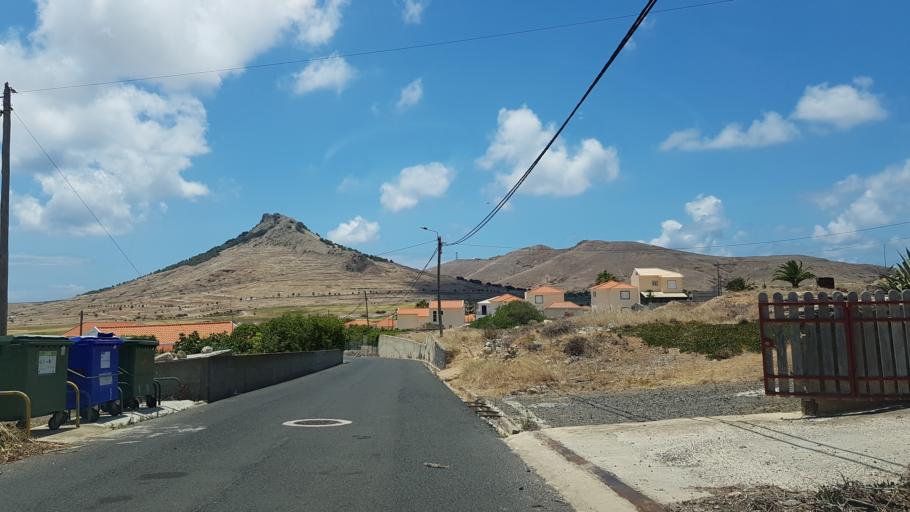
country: PT
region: Madeira
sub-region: Porto Santo
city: Vila de Porto Santo
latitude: 33.0572
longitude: -16.3608
